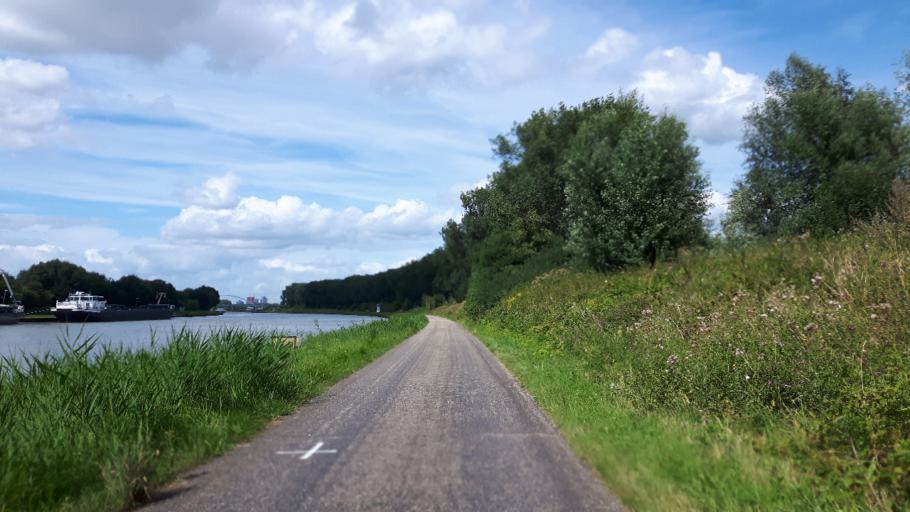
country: NL
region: Utrecht
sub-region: Gemeente Nieuwegein
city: Nieuwegein
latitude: 52.0245
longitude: 5.1150
